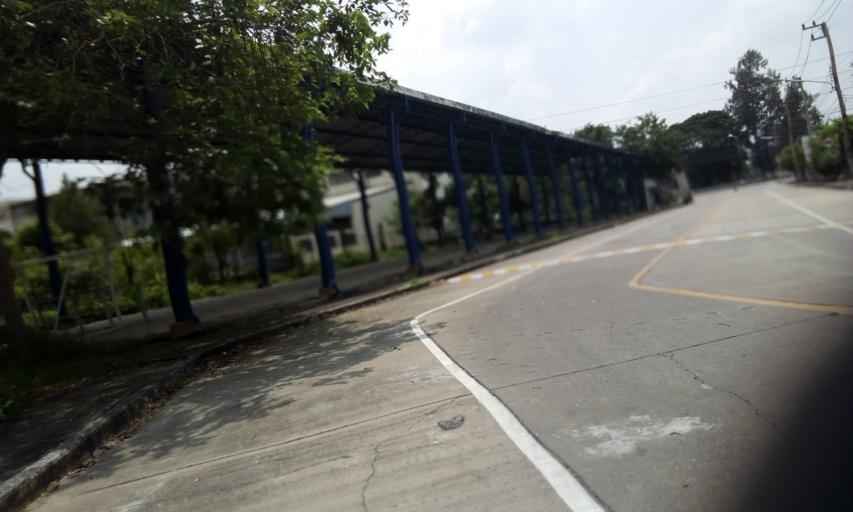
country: TH
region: Pathum Thani
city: Ban Rangsit
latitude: 14.0534
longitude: 100.8226
